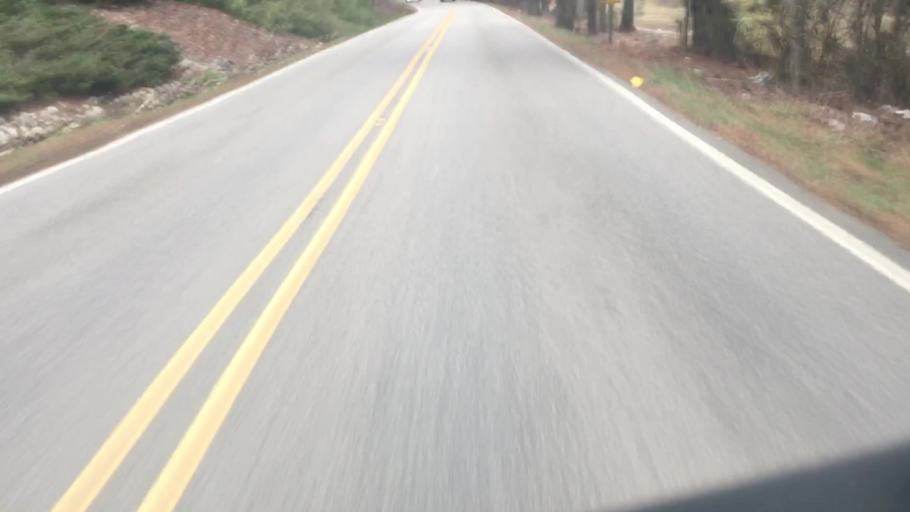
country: US
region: Alabama
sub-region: Jefferson County
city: Vestavia Hills
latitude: 33.4161
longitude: -86.7523
